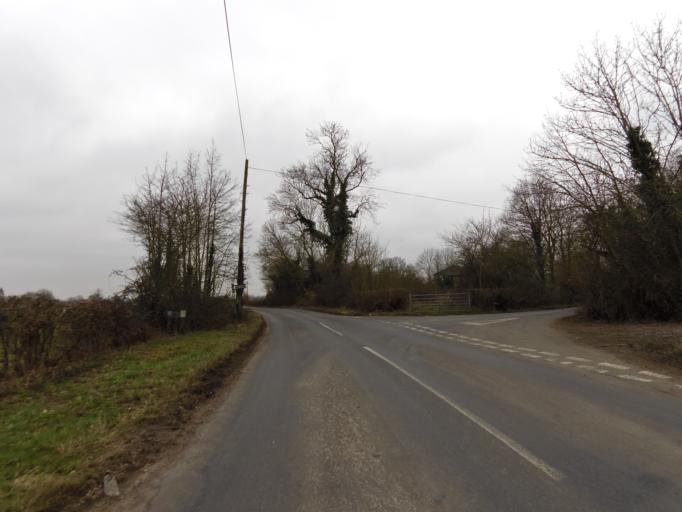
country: GB
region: England
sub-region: Suffolk
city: Framlingham
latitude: 52.2326
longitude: 1.3595
